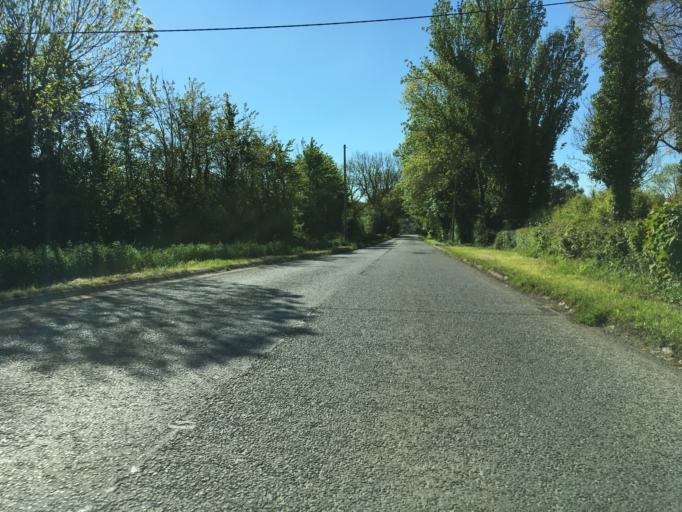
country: GB
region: England
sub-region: South Gloucestershire
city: Severn Beach
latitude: 51.5225
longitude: -2.6534
